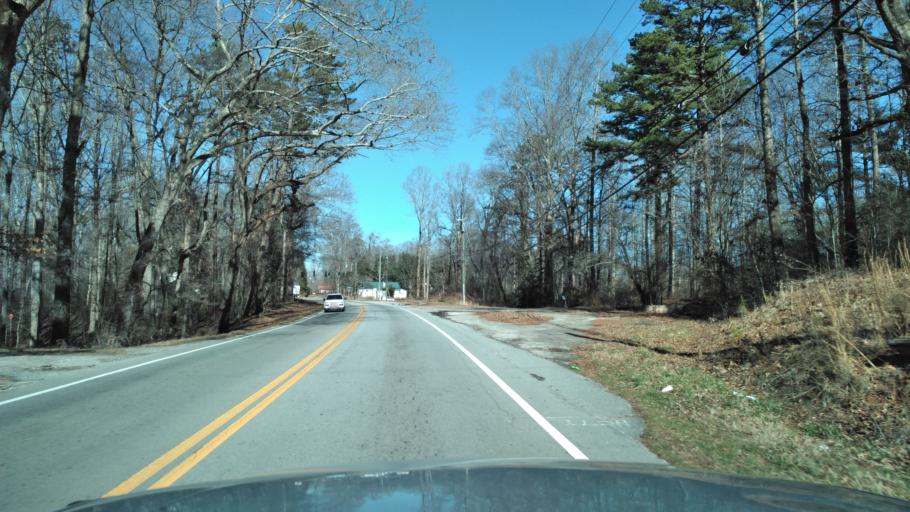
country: US
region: Georgia
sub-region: Hall County
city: Gainesville
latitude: 34.3165
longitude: -83.7602
